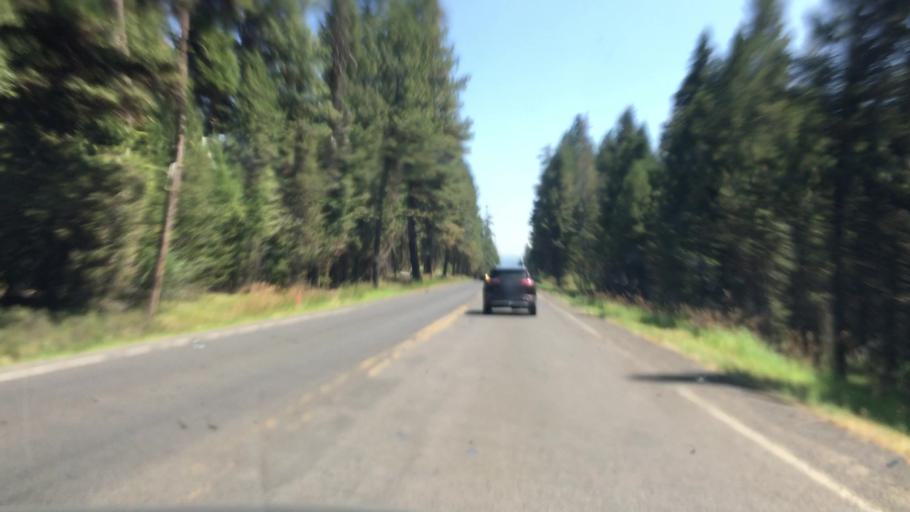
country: US
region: Idaho
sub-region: Valley County
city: McCall
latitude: 44.9238
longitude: -116.1410
